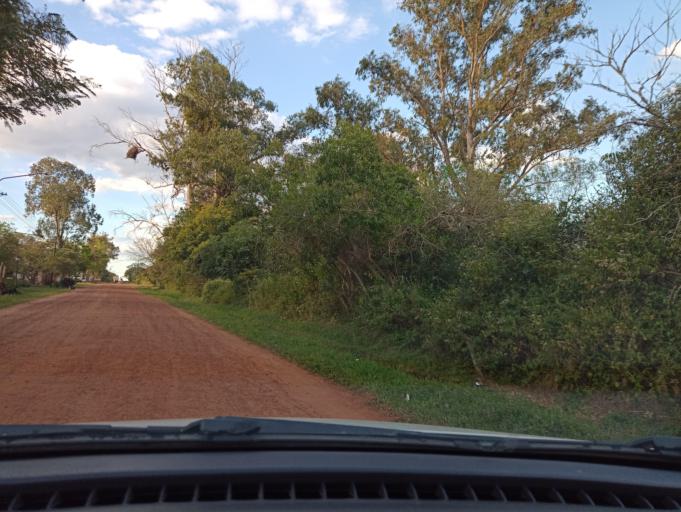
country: AR
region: Corrientes
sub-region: Departamento de San Miguel
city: San Miguel
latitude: -28.5361
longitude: -57.1731
